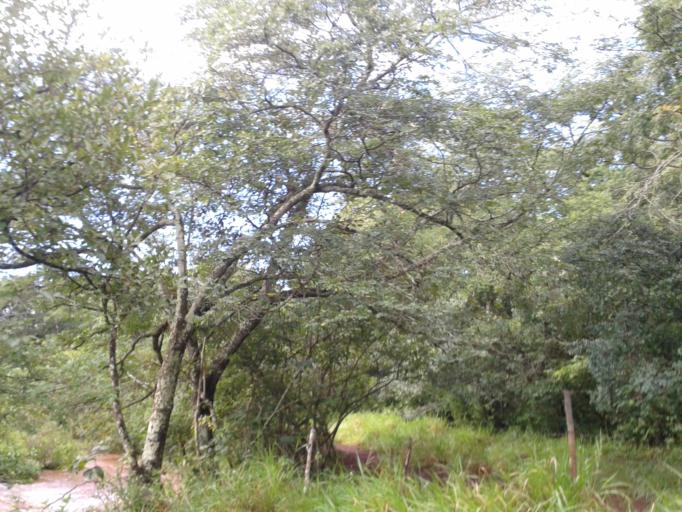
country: BR
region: Minas Gerais
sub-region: Ituiutaba
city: Ituiutaba
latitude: -18.9401
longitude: -49.3359
